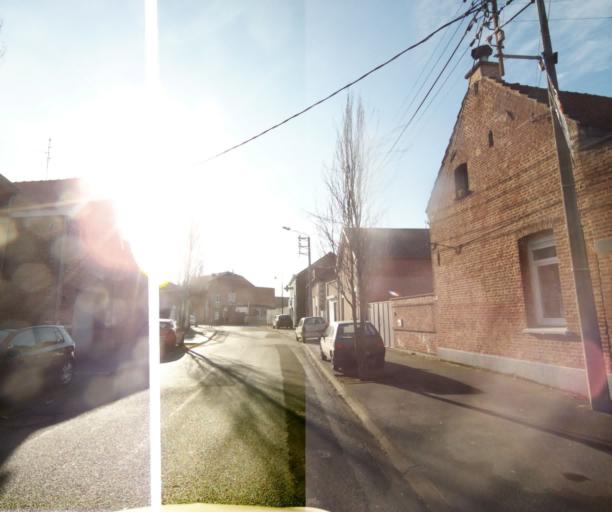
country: FR
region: Nord-Pas-de-Calais
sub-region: Departement du Nord
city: Maing
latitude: 50.3097
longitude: 3.4845
